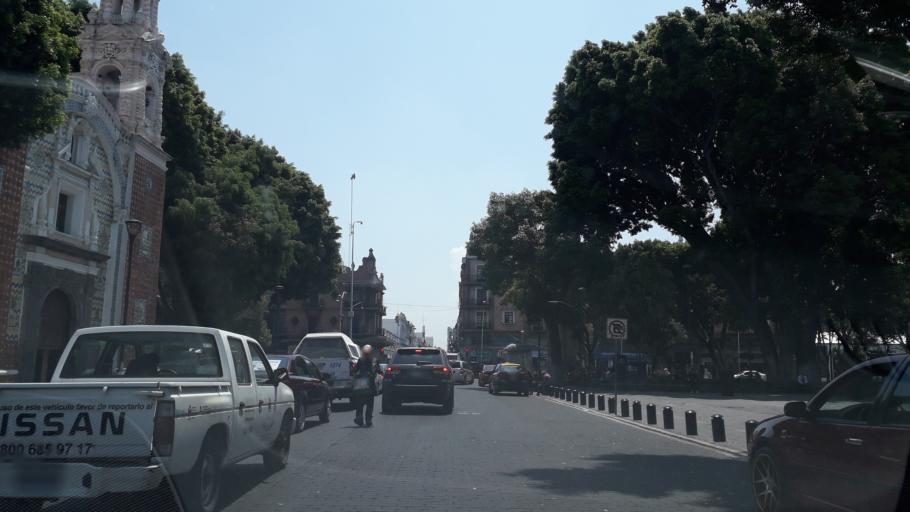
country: MX
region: Puebla
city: Puebla
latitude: 19.0487
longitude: -98.2070
